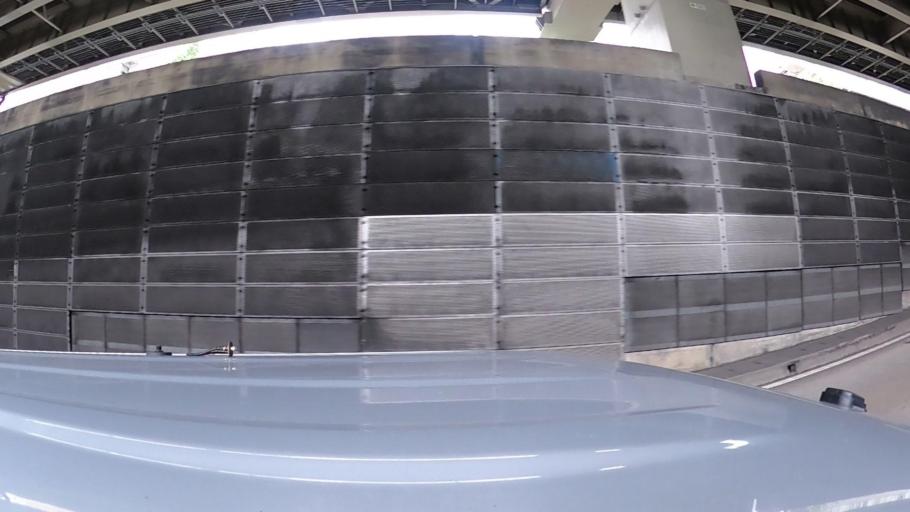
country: JP
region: Kanagawa
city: Yokohama
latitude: 35.4612
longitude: 139.6252
